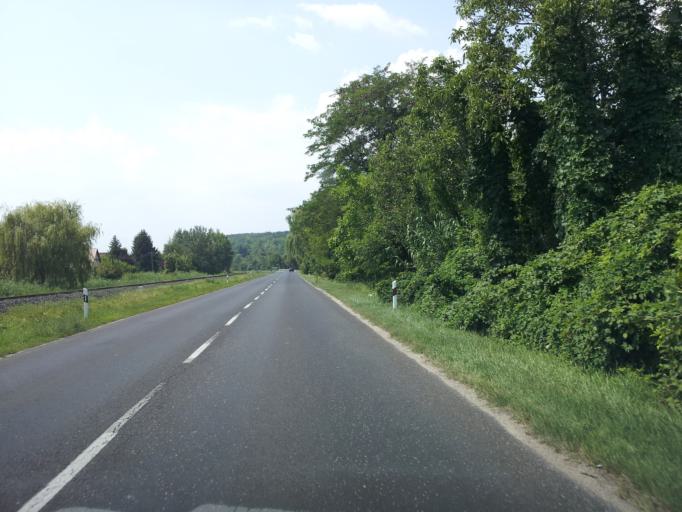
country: HU
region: Veszprem
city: Balatonkenese
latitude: 47.0366
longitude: 18.0871
